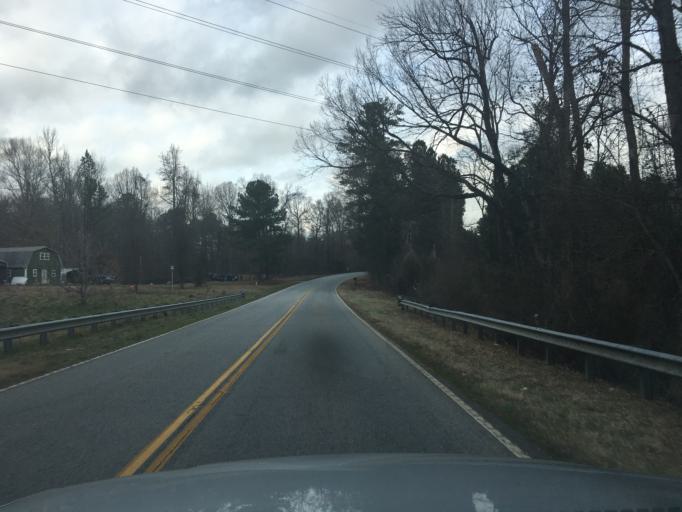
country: US
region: South Carolina
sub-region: Abbeville County
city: Abbeville
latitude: 34.2140
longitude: -82.3899
